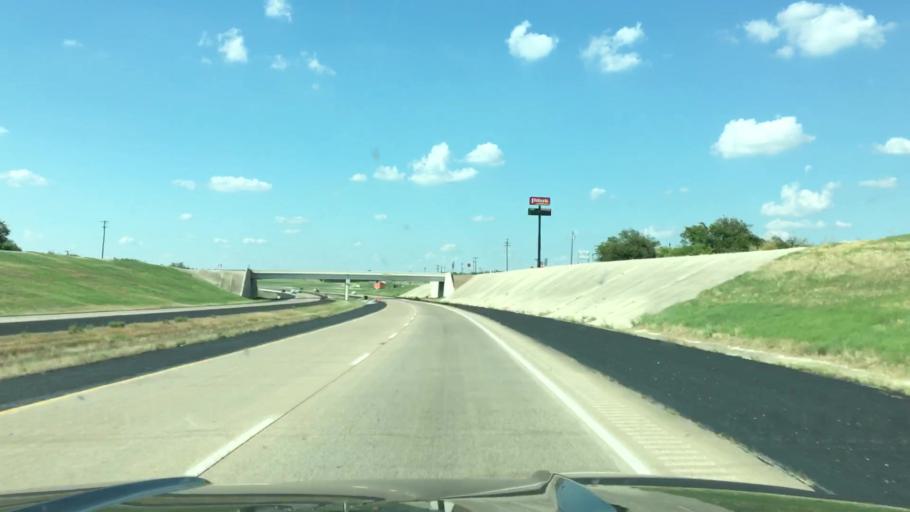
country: US
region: Texas
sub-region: Wise County
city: New Fairview
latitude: 33.0976
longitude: -97.4709
